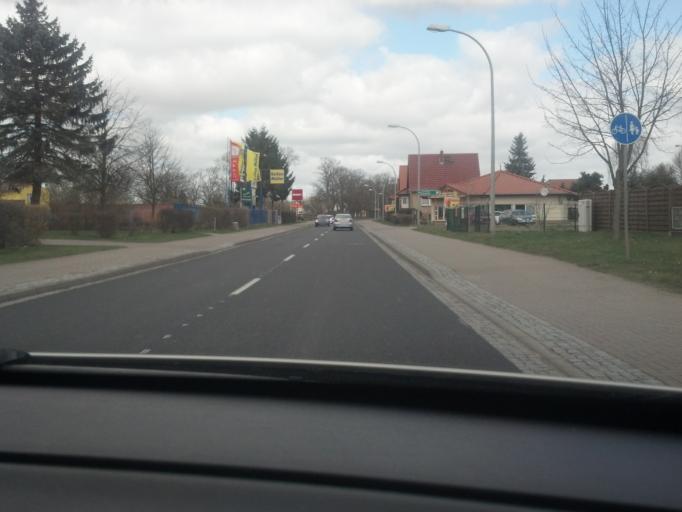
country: DE
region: Brandenburg
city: Gerdshagen
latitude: 53.3190
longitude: 12.2407
